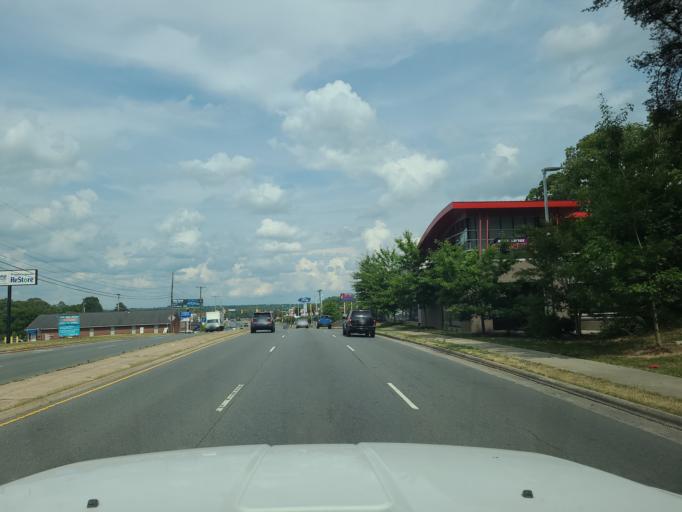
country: US
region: North Carolina
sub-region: Gaston County
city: Ranlo
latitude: 35.2614
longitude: -81.1463
